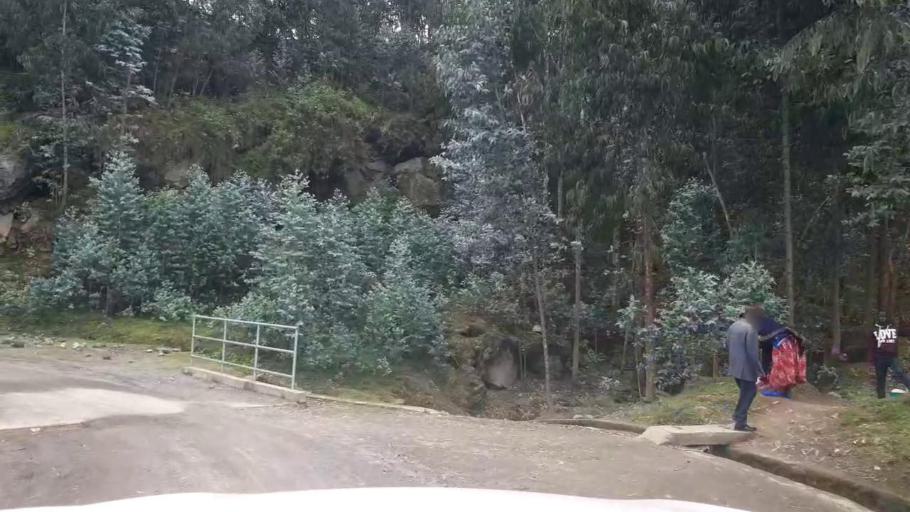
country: RW
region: Northern Province
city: Musanze
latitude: -1.5401
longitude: 29.5339
